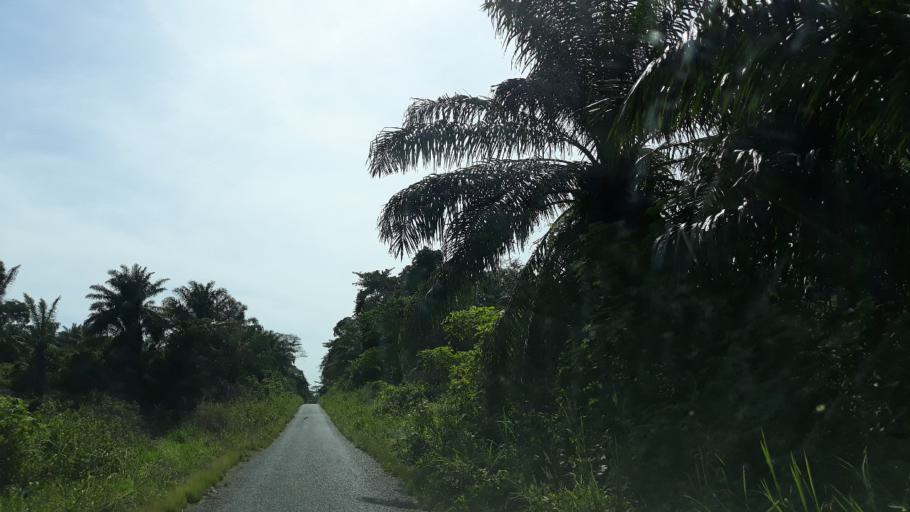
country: CD
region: Maniema
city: Kindu
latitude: -2.9052
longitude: 26.0334
